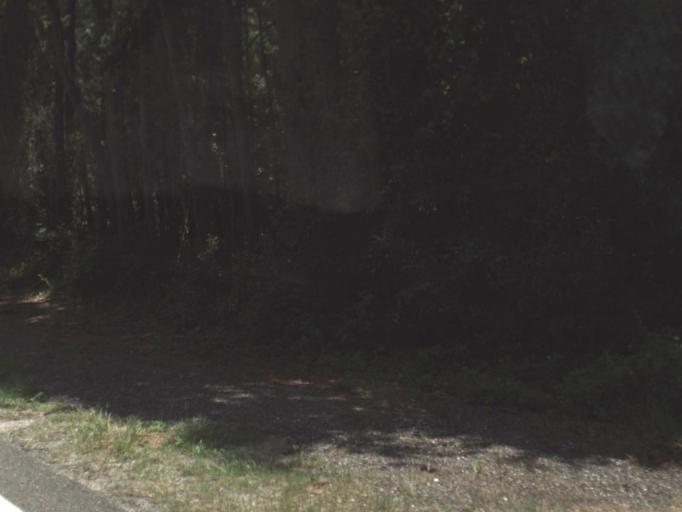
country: US
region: Florida
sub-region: Clay County
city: Keystone Heights
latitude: 29.7741
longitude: -82.0515
